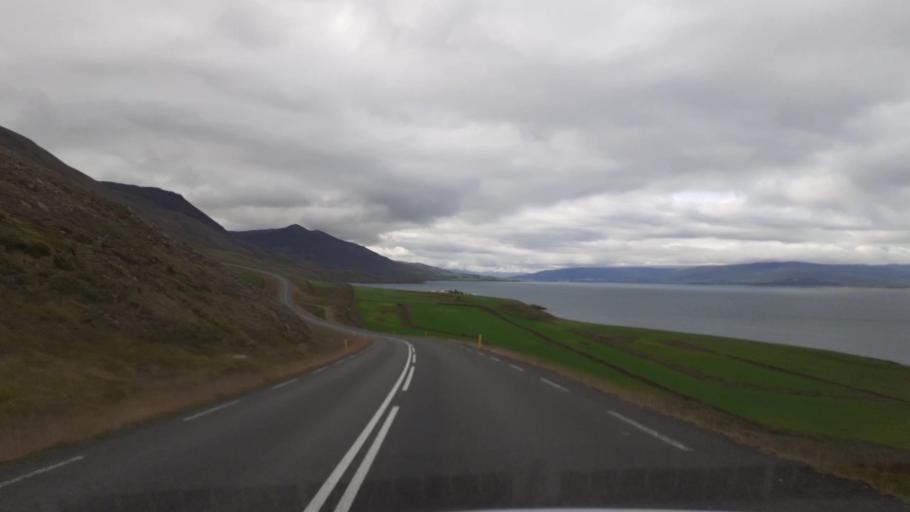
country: IS
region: Northeast
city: Akureyri
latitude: 65.8688
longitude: -18.0760
